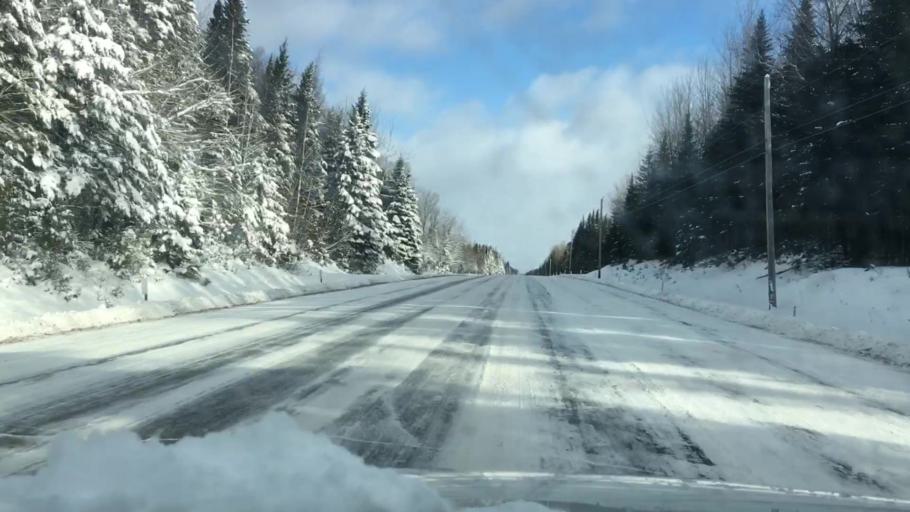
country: US
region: Maine
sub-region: Aroostook County
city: Van Buren
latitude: 47.0502
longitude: -67.9973
